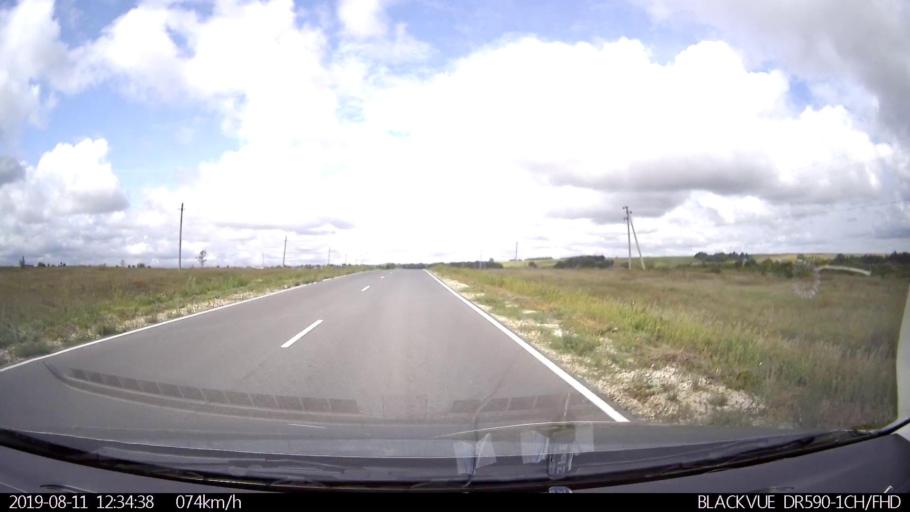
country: RU
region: Ulyanovsk
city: Ignatovka
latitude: 53.8183
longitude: 47.8402
